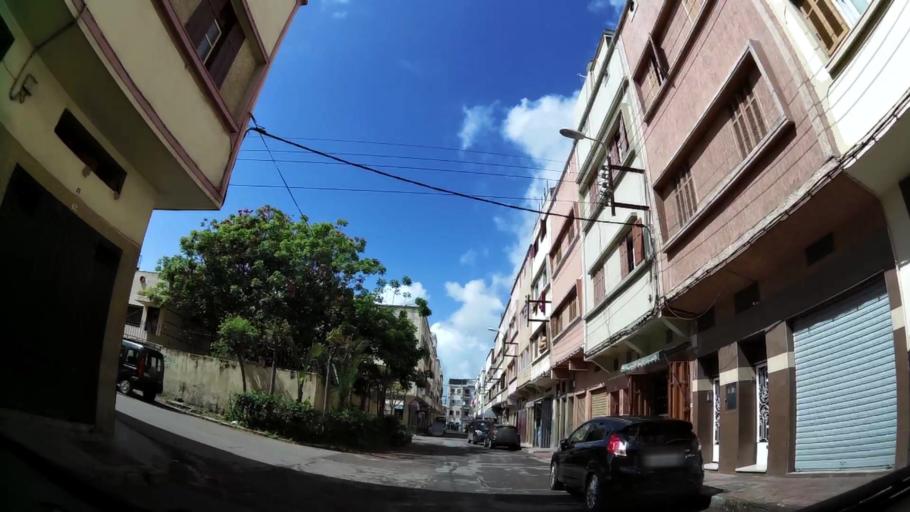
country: MA
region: Grand Casablanca
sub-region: Casablanca
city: Casablanca
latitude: 33.5408
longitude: -7.5834
